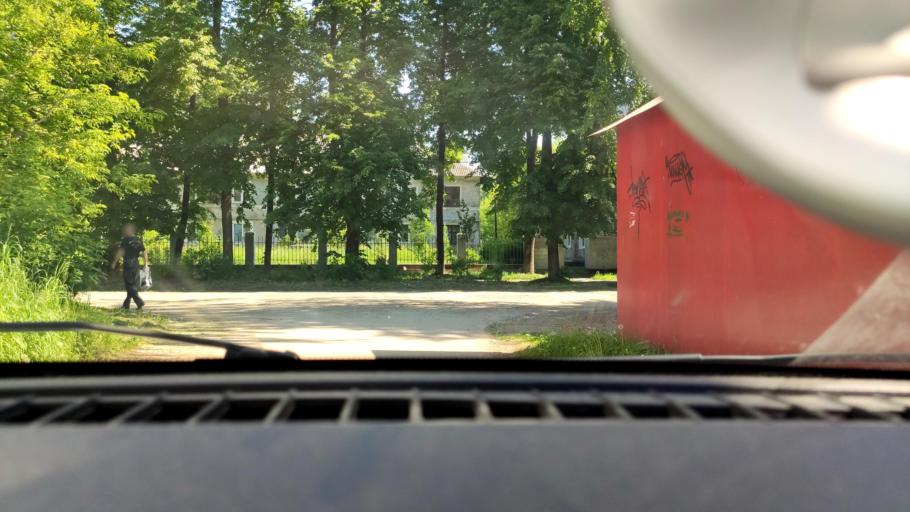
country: RU
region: Perm
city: Perm
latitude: 58.1117
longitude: 56.3138
